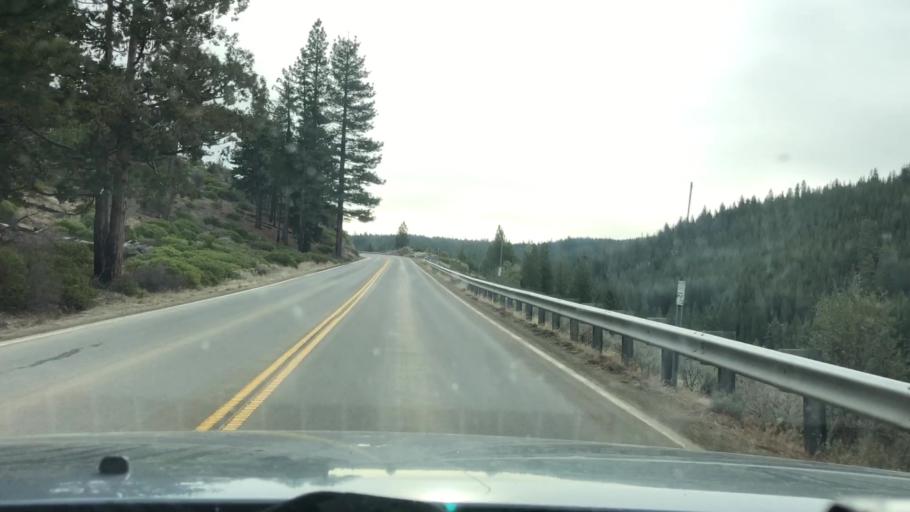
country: US
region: California
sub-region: Plumas County
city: Portola
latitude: 39.5588
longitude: -120.3477
